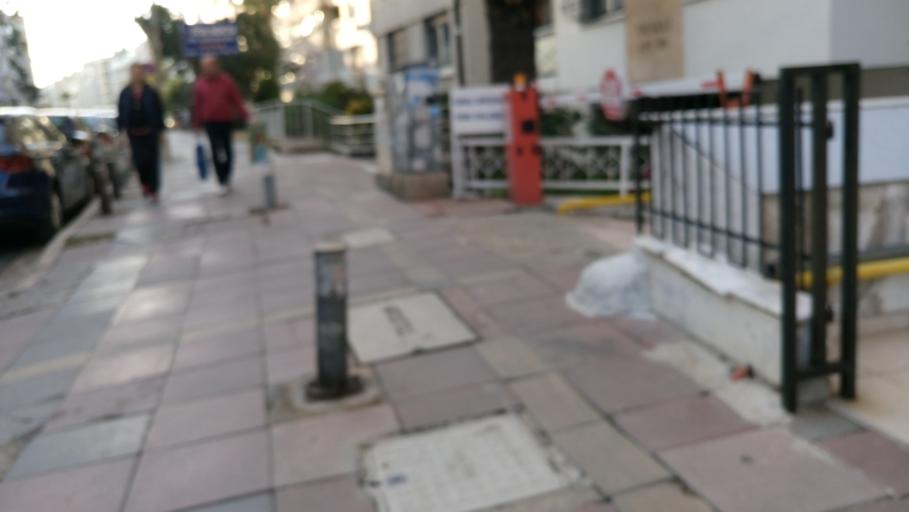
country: TR
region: Izmir
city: Izmir
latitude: 38.4061
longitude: 27.1015
